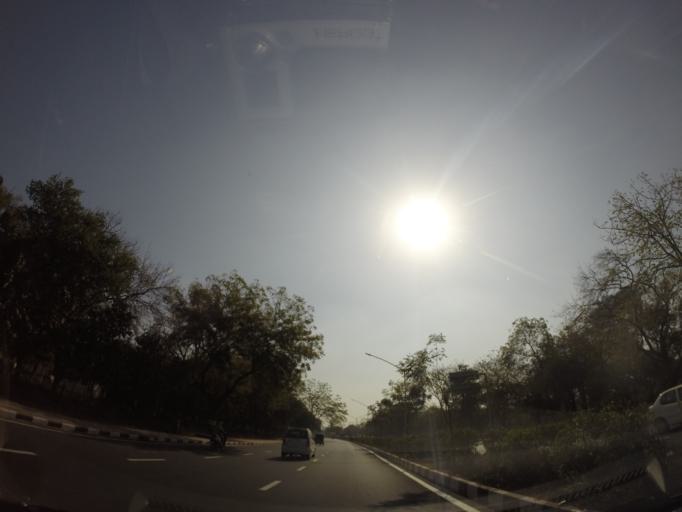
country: IN
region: Gujarat
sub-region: Gandhinagar
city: Ghandinagar
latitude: 23.1995
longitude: 72.6317
